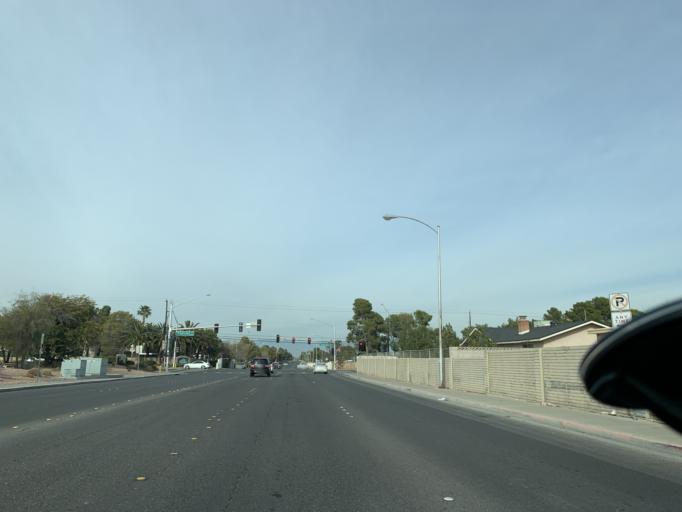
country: US
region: Nevada
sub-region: Clark County
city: Spring Valley
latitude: 36.0990
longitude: -115.2340
